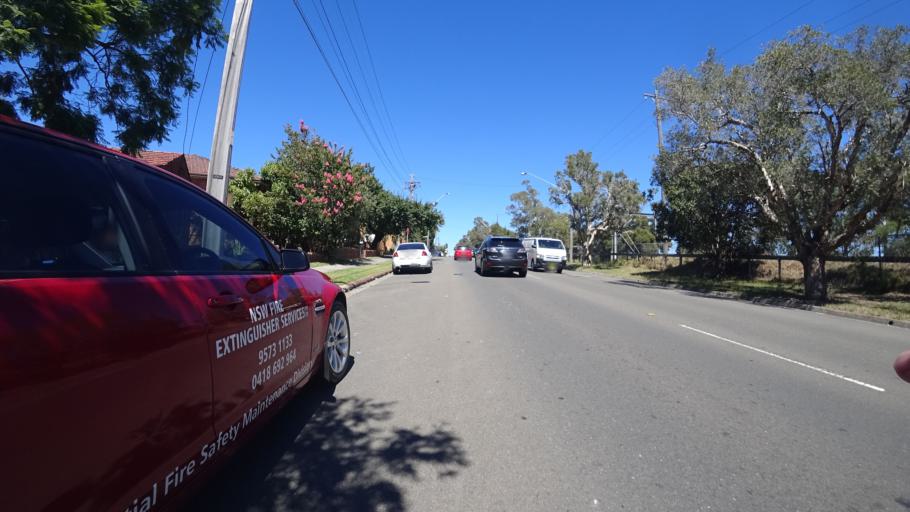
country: AU
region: New South Wales
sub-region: Kogarah
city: Kogarah Bay
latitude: -33.9695
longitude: 151.1198
